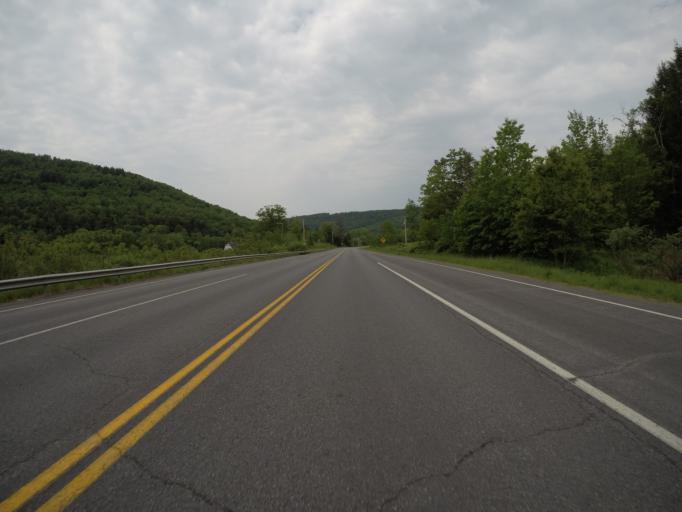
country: US
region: New York
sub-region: Sullivan County
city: Livingston Manor
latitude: 41.9678
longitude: -74.9003
